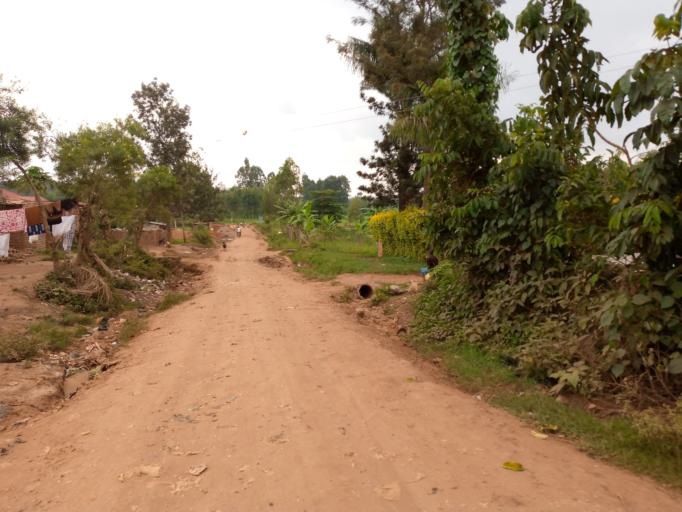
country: UG
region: Eastern Region
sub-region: Mbale District
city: Mbale
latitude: 1.0885
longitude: 34.1639
